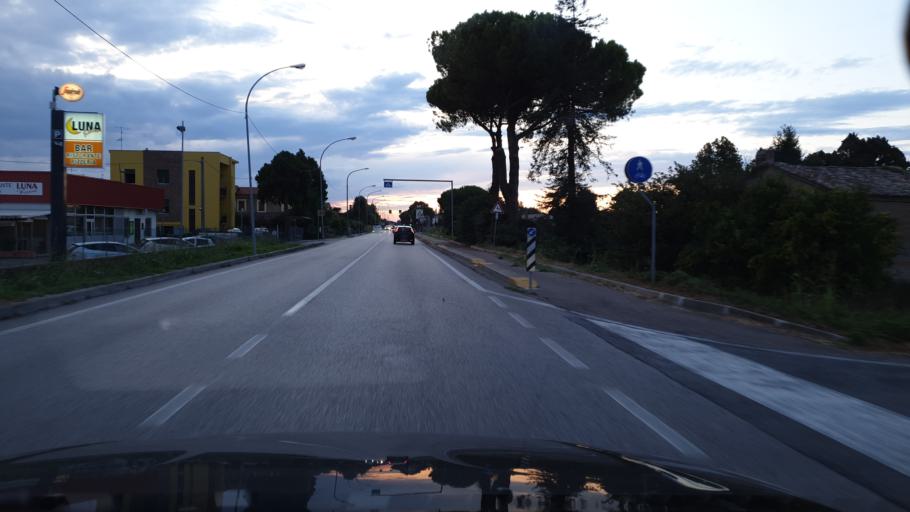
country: IT
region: Emilia-Romagna
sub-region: Provincia di Ravenna
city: Fornace Zarattini
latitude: 44.4474
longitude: 12.1260
